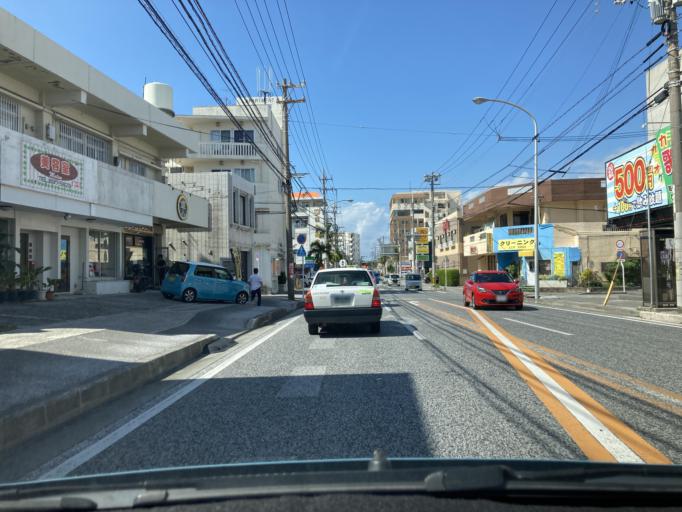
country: JP
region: Okinawa
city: Ginowan
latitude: 26.2615
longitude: 127.7426
